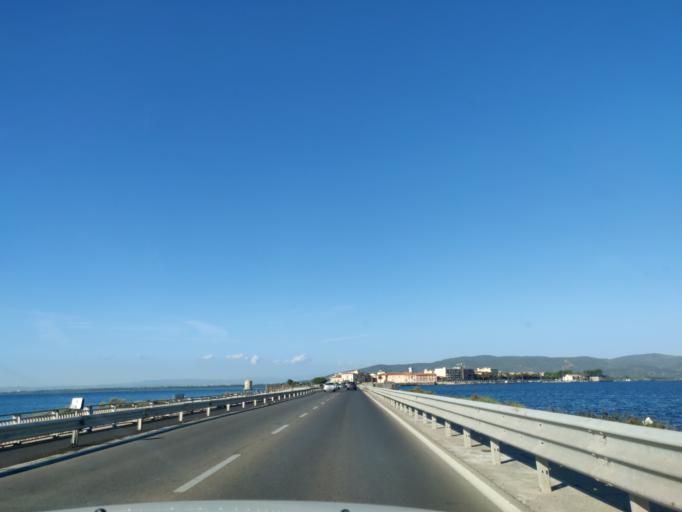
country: IT
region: Tuscany
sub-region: Provincia di Grosseto
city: Orbetello
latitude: 42.4319
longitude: 11.2023
